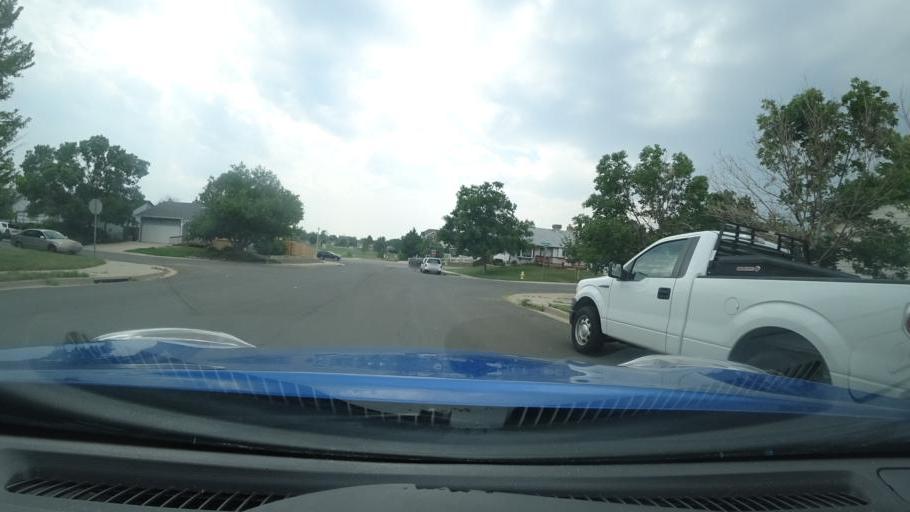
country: US
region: Colorado
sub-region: Adams County
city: Aurora
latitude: 39.6871
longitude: -104.7619
